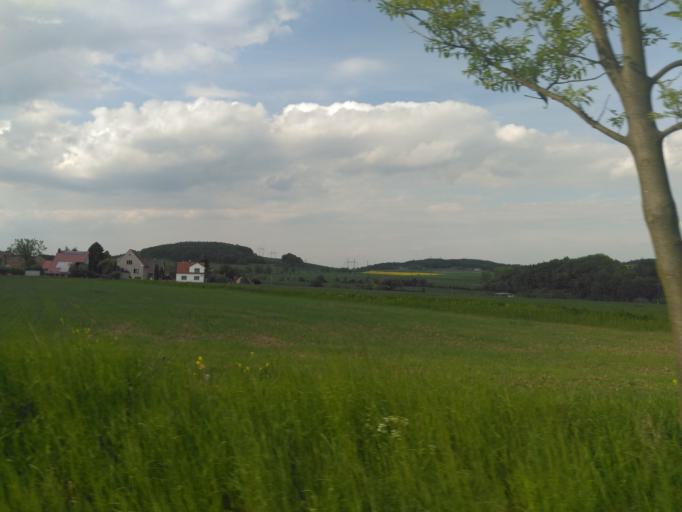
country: CZ
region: Central Bohemia
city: Chynava
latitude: 50.0068
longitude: 14.0933
